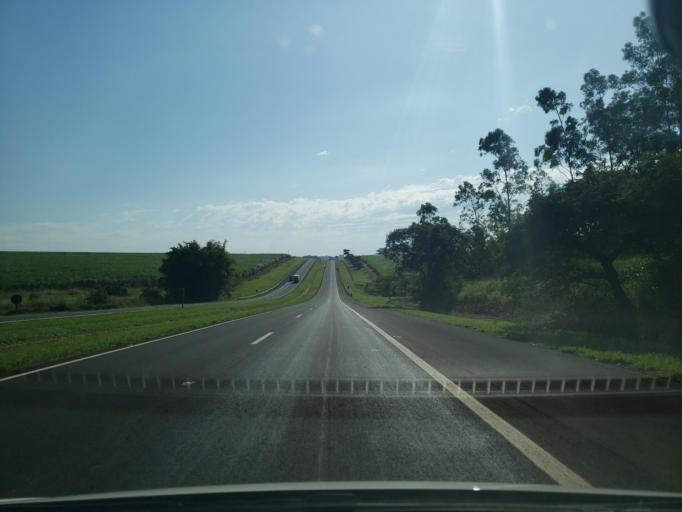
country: BR
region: Sao Paulo
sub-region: Promissao
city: Promissao
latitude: -21.5359
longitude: -49.9774
